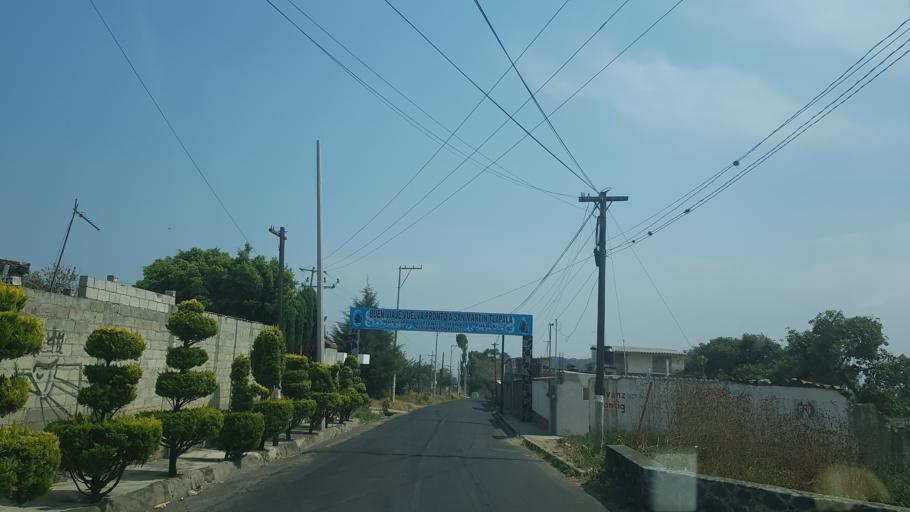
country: MX
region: Puebla
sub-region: Tianguismanalco
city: San Martin Tlapala
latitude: 18.9624
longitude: -98.4595
